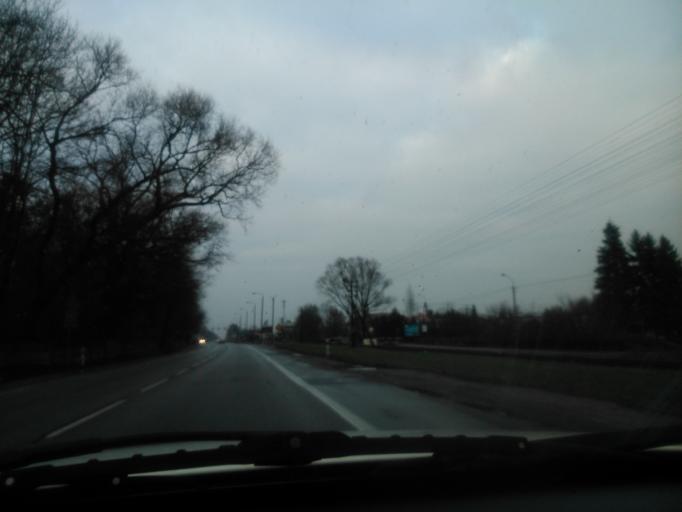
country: PL
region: Kujawsko-Pomorskie
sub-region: Powiat torunski
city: Lysomice
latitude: 53.0834
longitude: 18.6194
